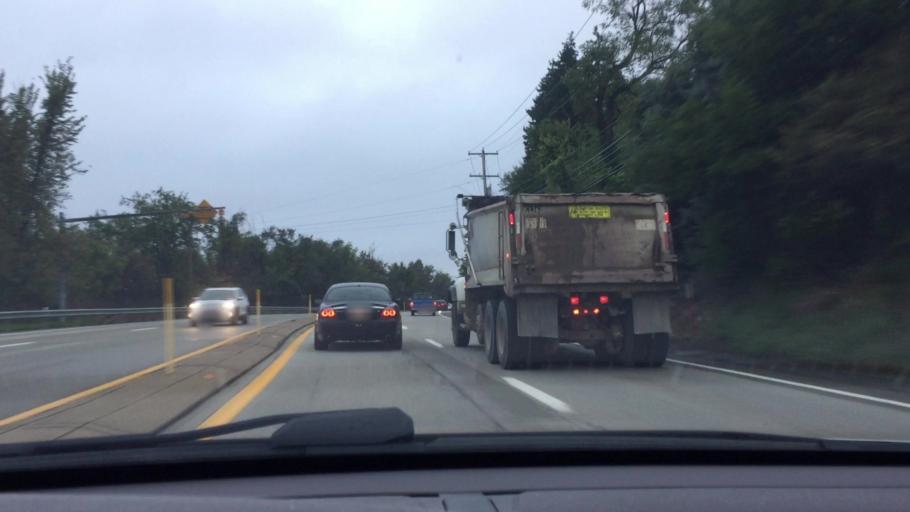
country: US
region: Pennsylvania
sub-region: Washington County
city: East Washington
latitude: 40.1924
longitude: -80.2122
